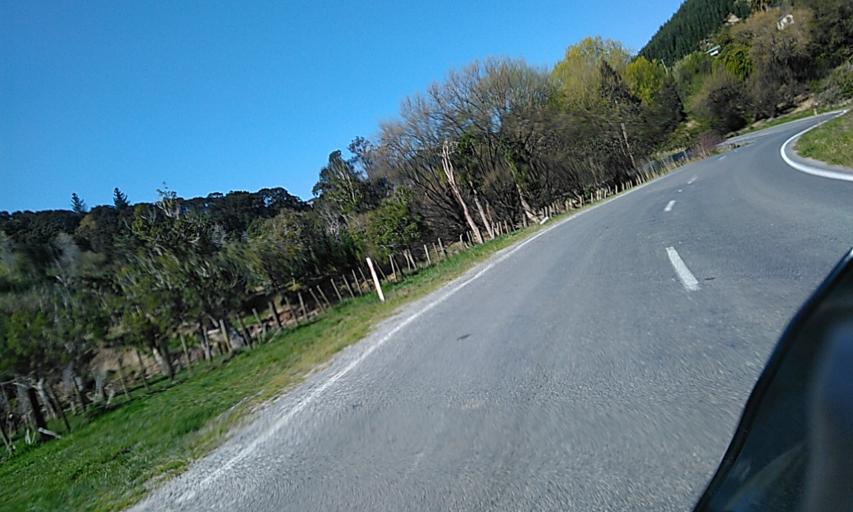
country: NZ
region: Gisborne
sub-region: Gisborne District
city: Gisborne
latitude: -38.3268
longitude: 178.1667
